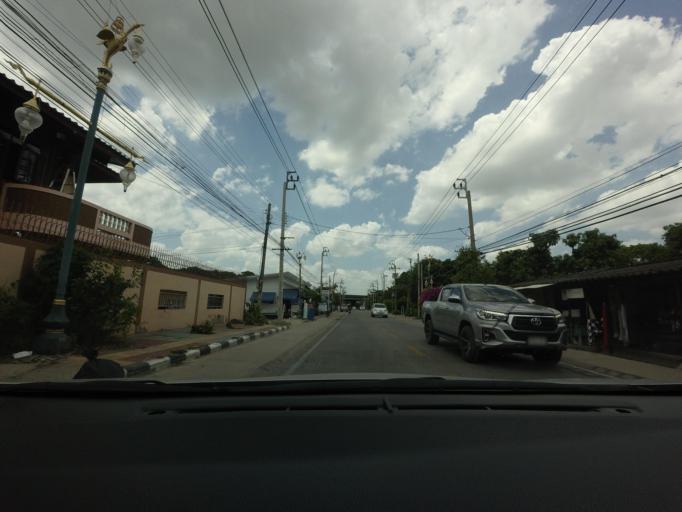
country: TH
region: Samut Prakan
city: Phra Pradaeng
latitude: 13.6360
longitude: 100.5598
